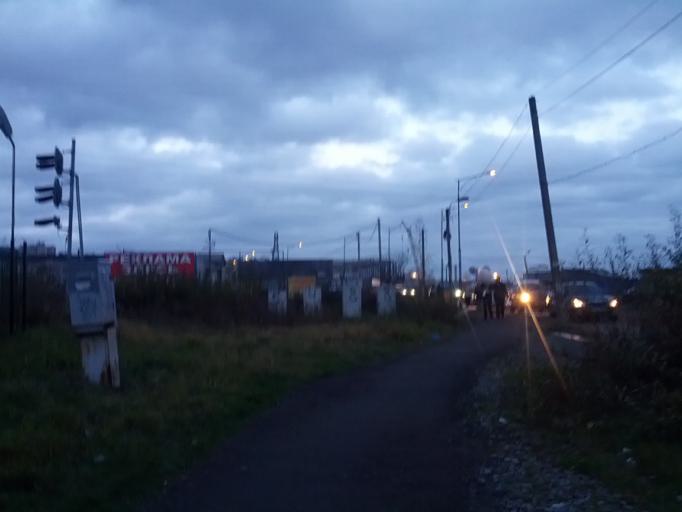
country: RU
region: Leningrad
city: Rybatskoye
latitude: 59.8964
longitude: 30.4963
